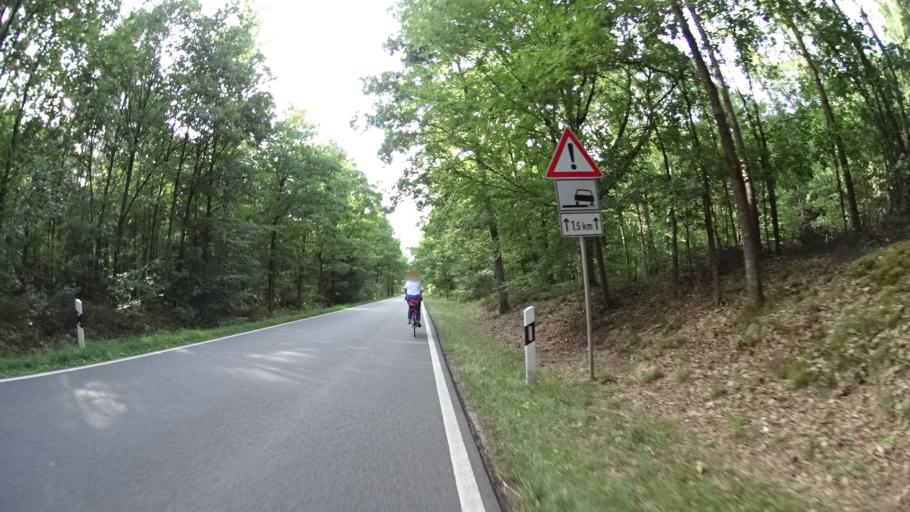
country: DE
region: Lower Saxony
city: Handeloh
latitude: 53.1740
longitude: 9.8889
